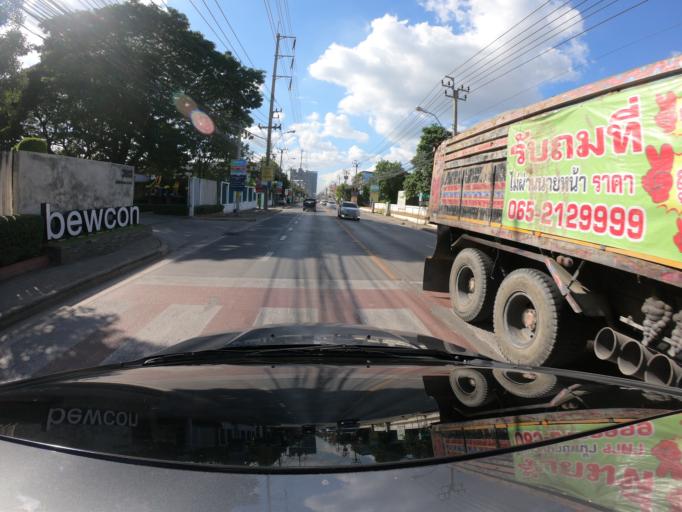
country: TH
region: Bangkok
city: Bang Na
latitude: 13.6548
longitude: 100.6110
